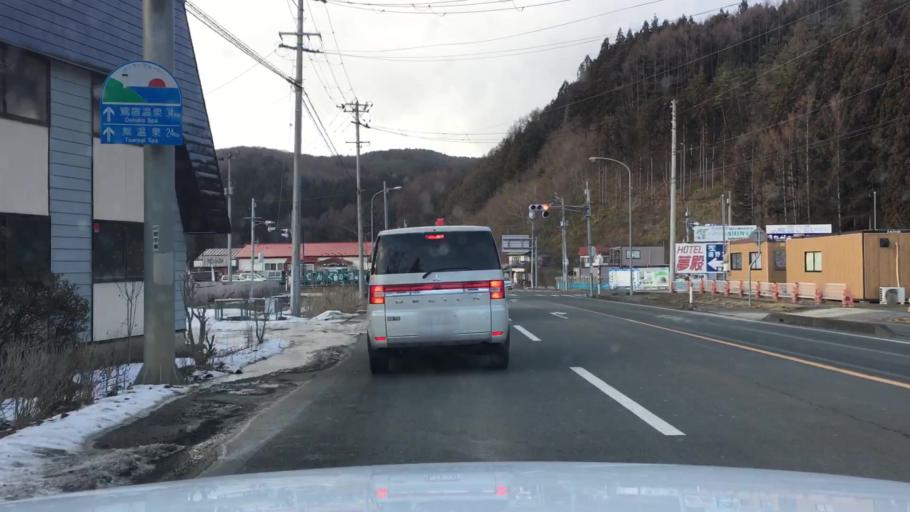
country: JP
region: Iwate
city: Morioka-shi
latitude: 39.6740
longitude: 141.2108
